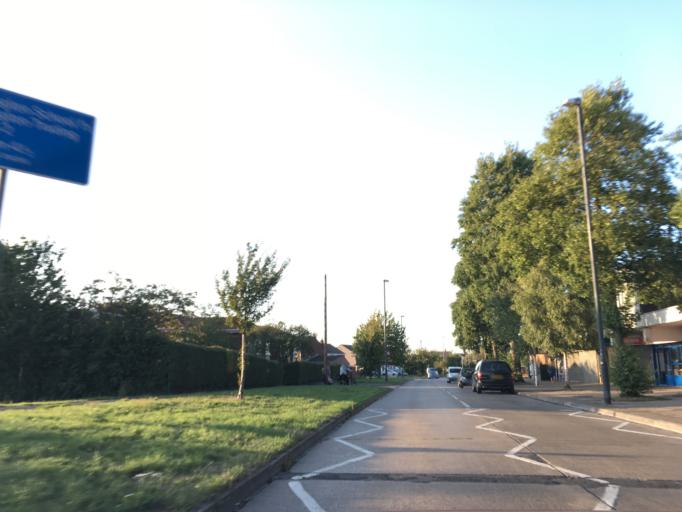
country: GB
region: England
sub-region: Bath and North East Somerset
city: Whitchurch
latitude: 51.4119
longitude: -2.5476
